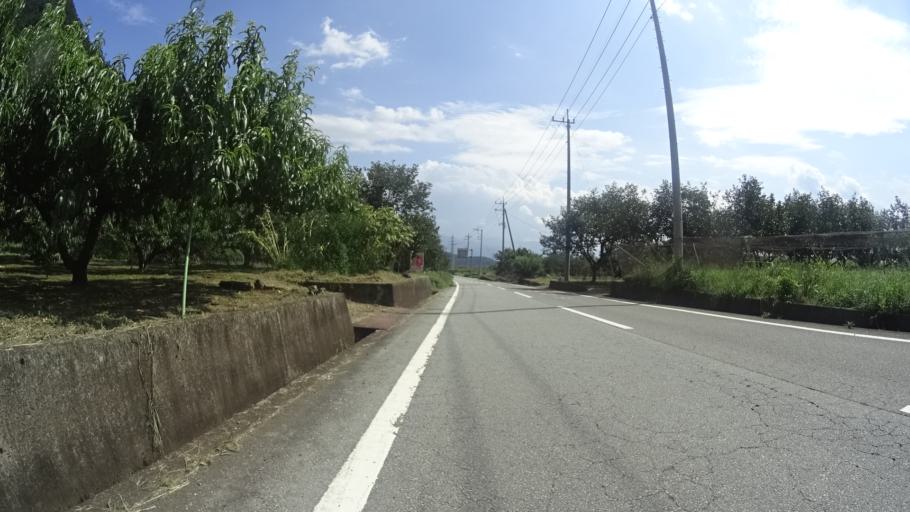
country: JP
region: Yamanashi
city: Enzan
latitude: 35.7381
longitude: 138.7213
